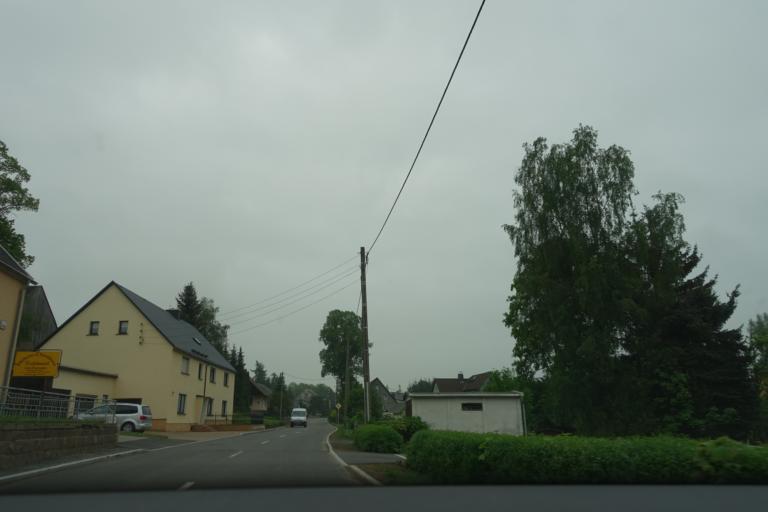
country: DE
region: Saxony
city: Brand-Erbisdorf
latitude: 50.8319
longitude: 13.2977
